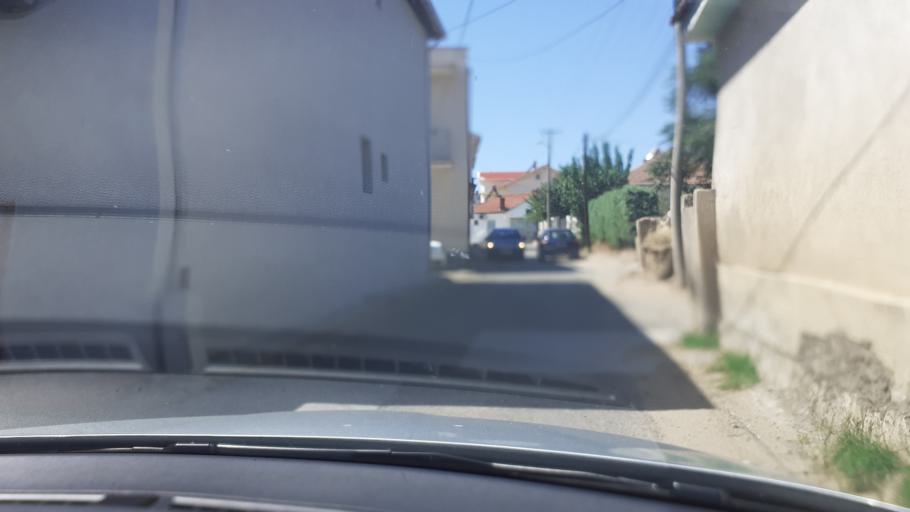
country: MK
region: Bogdanci
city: Bogdanci
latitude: 41.2000
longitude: 22.5753
